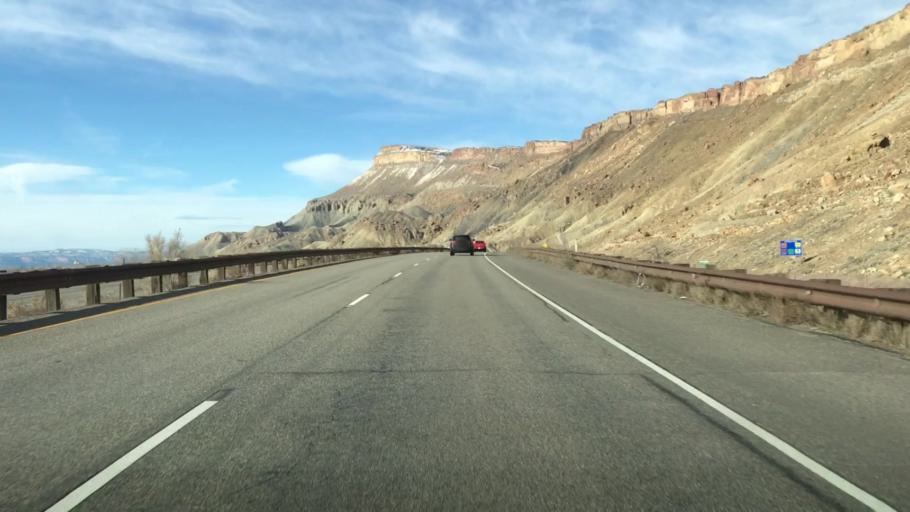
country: US
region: Colorado
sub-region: Mesa County
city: Palisade
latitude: 39.1173
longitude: -108.3572
